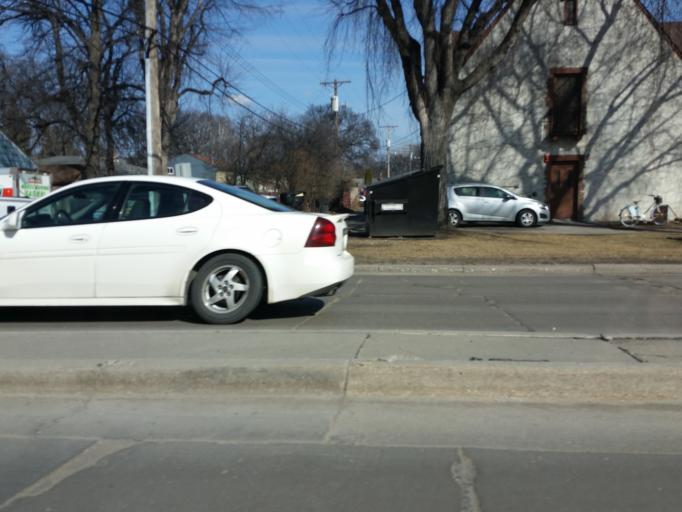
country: US
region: North Dakota
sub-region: Grand Forks County
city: Grand Forks
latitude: 47.9227
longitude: -97.0666
